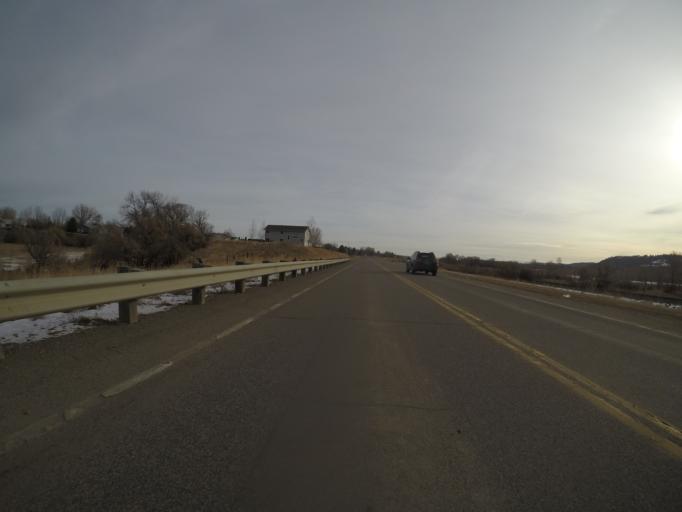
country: US
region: Montana
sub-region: Stillwater County
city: Columbus
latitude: 45.6409
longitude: -109.2707
